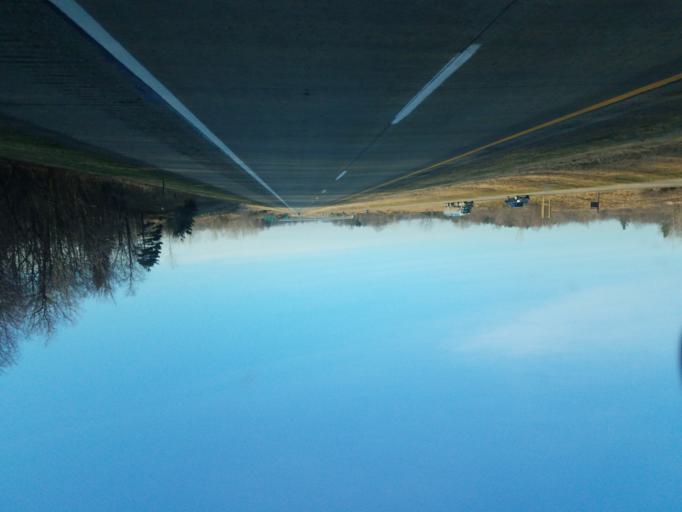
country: US
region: Michigan
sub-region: Clinton County
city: DeWitt
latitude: 42.9016
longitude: -84.5174
